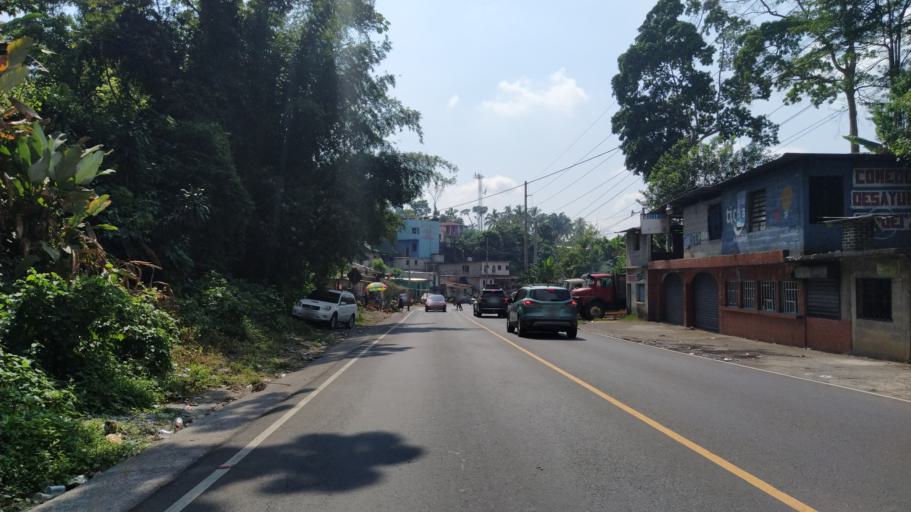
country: GT
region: Quetzaltenango
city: El Palmar
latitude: 14.6361
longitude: -91.5765
